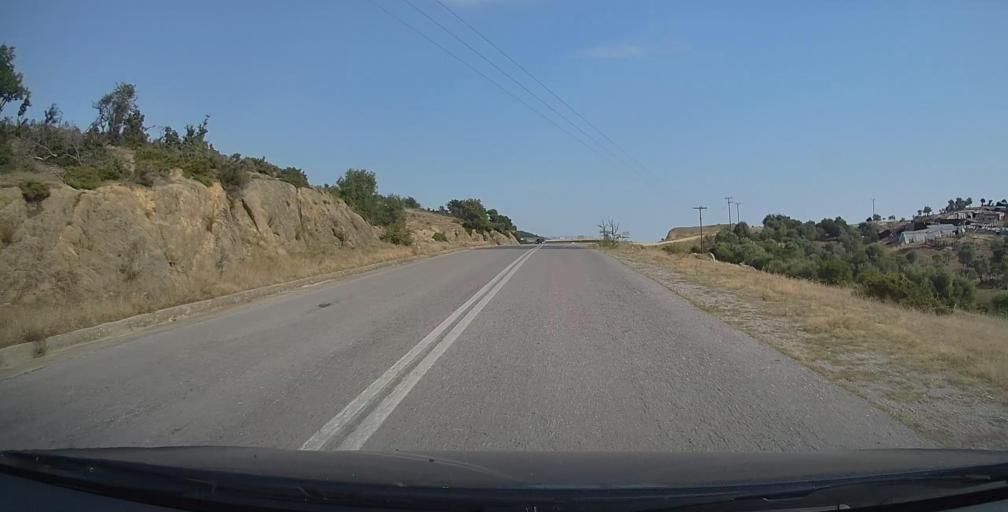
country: GR
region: Central Macedonia
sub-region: Nomos Chalkidikis
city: Sykia
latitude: 40.0170
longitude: 23.9868
